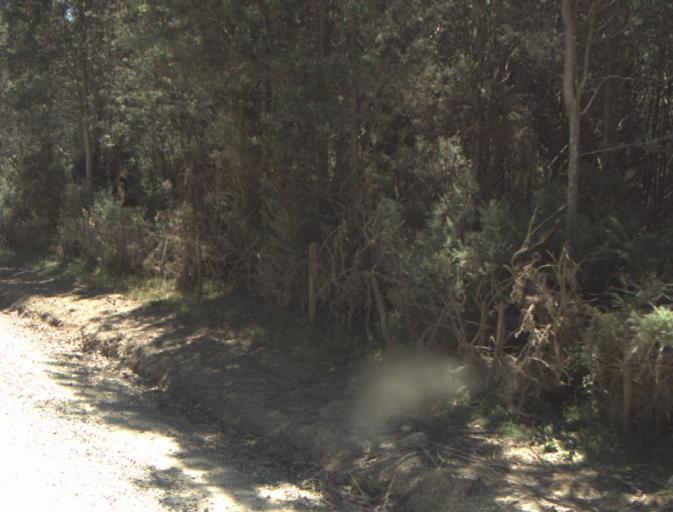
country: AU
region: Tasmania
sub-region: Dorset
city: Scottsdale
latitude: -41.3249
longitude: 147.4750
